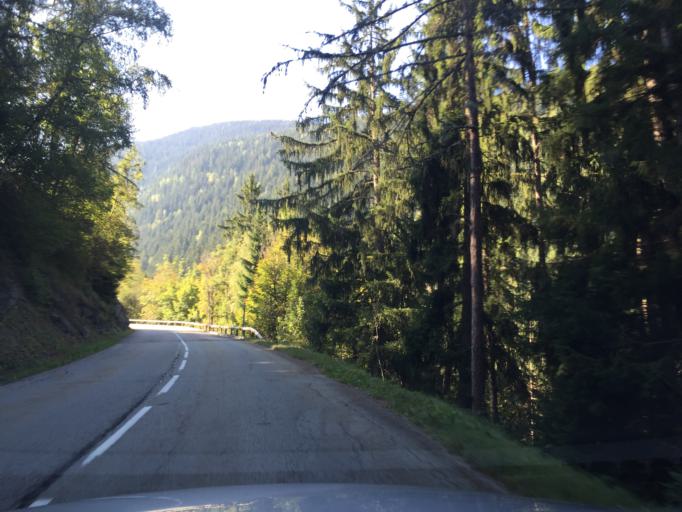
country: FR
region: Rhone-Alpes
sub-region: Departement de la Savoie
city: Bourg-Saint-Maurice
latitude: 45.5606
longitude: 6.7470
